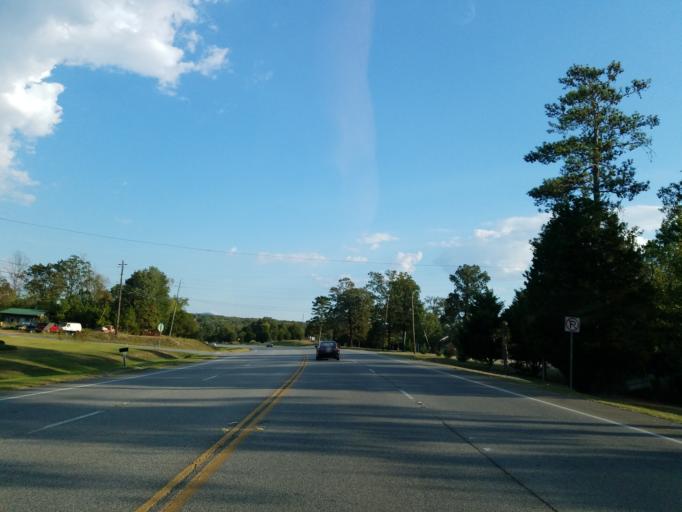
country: US
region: Georgia
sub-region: Murray County
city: Chatsworth
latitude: 34.7396
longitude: -84.7627
